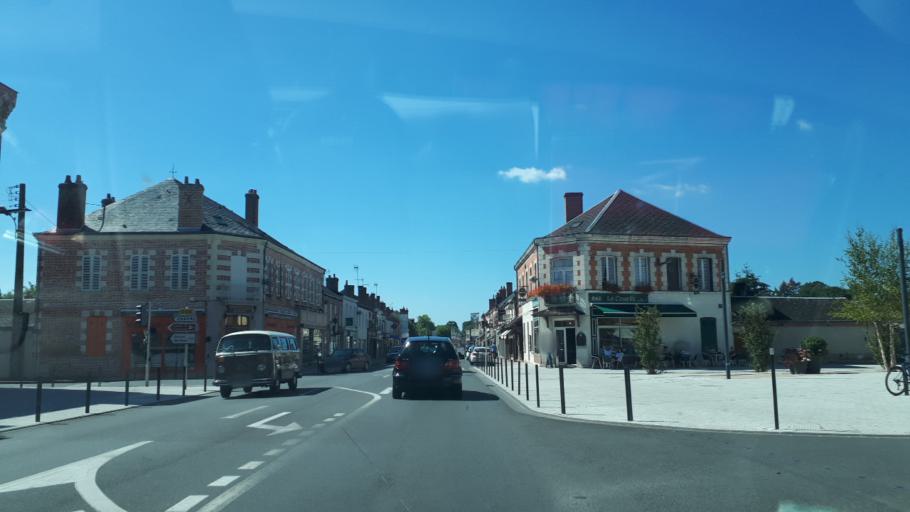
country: FR
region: Centre
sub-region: Departement du Loir-et-Cher
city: Lamotte-Beuvron
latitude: 47.6018
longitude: 2.0251
